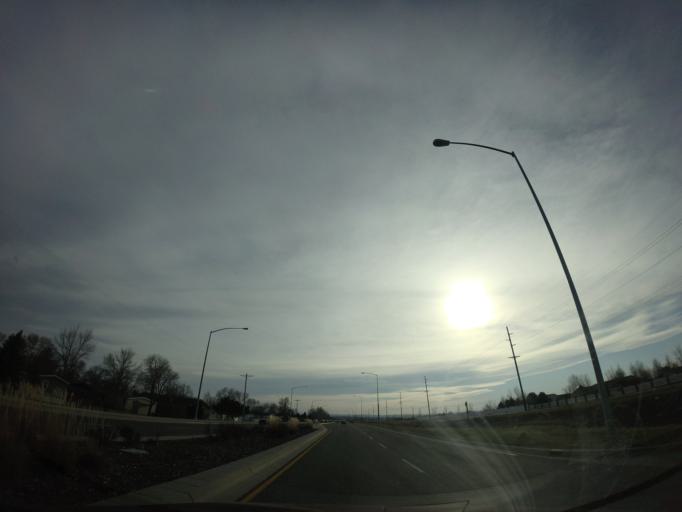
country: US
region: Montana
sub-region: Yellowstone County
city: Billings
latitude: 45.7663
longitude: -108.6176
